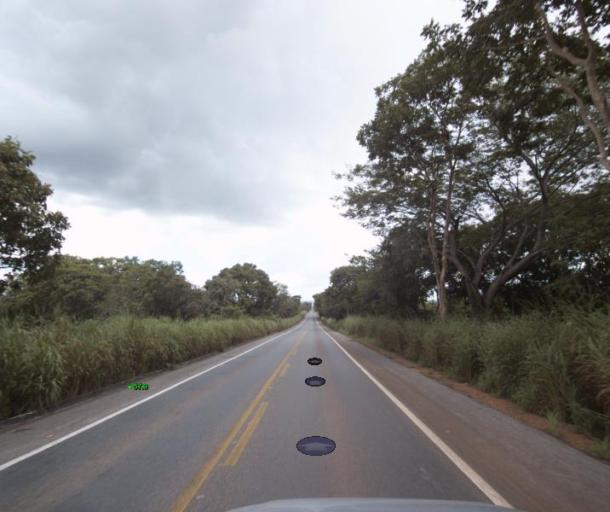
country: BR
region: Goias
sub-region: Porangatu
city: Porangatu
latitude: -13.3222
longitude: -49.1188
